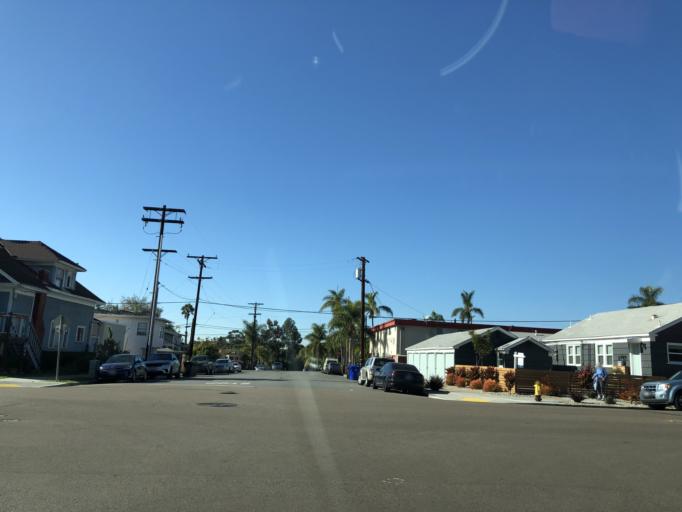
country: US
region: California
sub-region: San Diego County
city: San Diego
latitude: 32.7276
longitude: -117.1300
